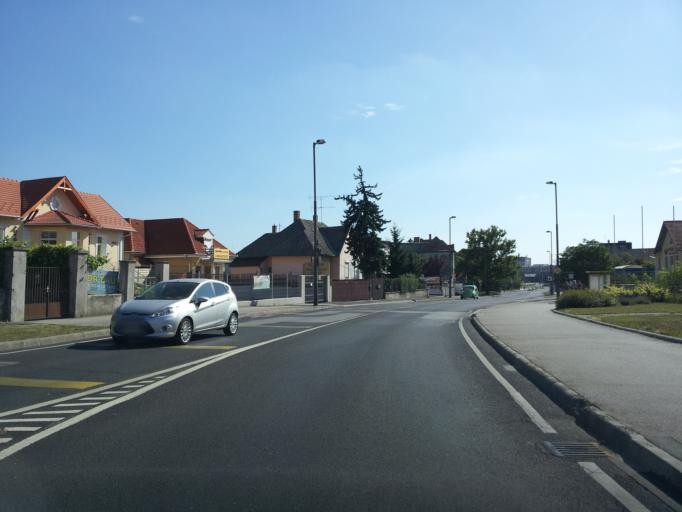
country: HU
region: Veszprem
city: Veszprem
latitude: 47.0953
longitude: 17.9182
